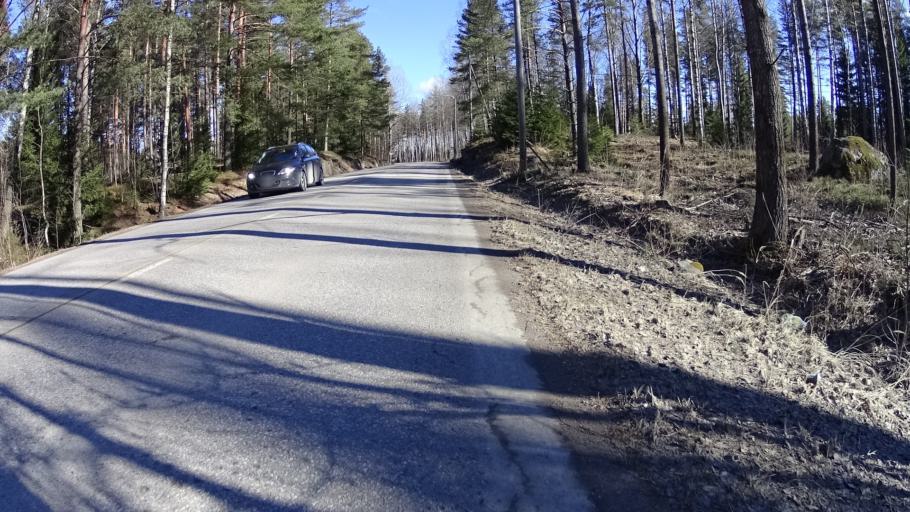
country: FI
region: Uusimaa
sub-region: Helsinki
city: Kauniainen
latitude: 60.2668
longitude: 24.7076
